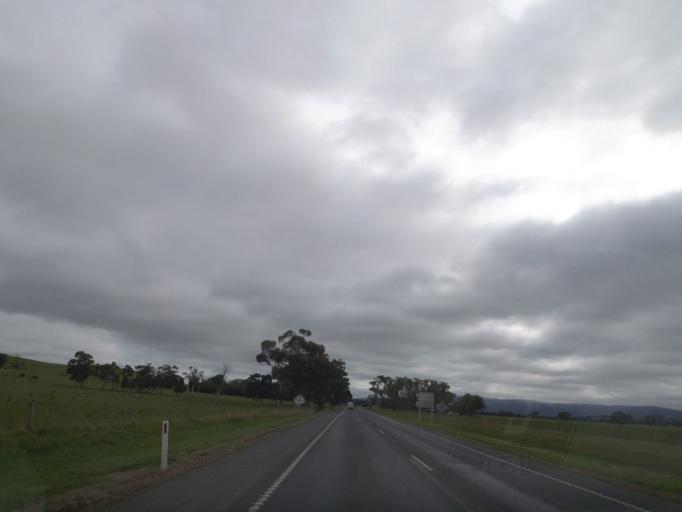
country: AU
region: Victoria
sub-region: Whittlesea
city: Whittlesea
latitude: -37.5558
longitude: 145.1095
